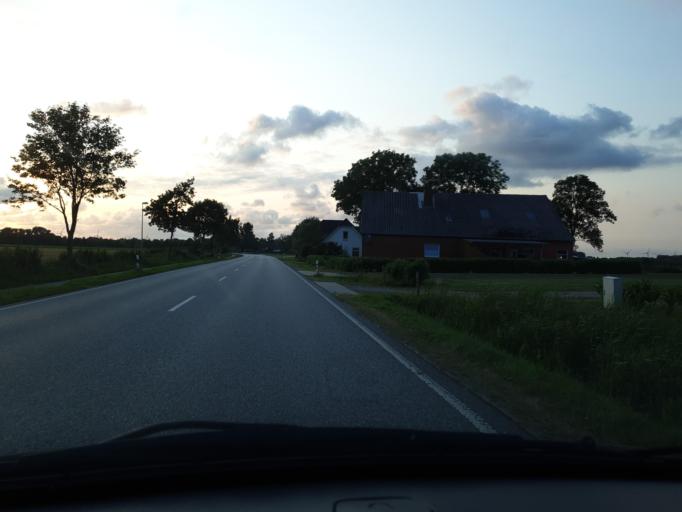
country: DE
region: Schleswig-Holstein
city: Diekhusen-Fahrstedt
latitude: 53.9388
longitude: 9.0266
